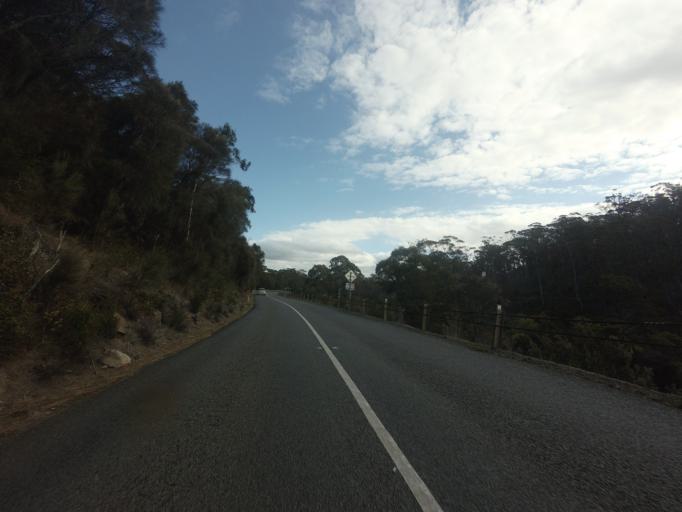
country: AU
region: Tasmania
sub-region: Sorell
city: Sorell
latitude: -42.5682
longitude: 147.8229
